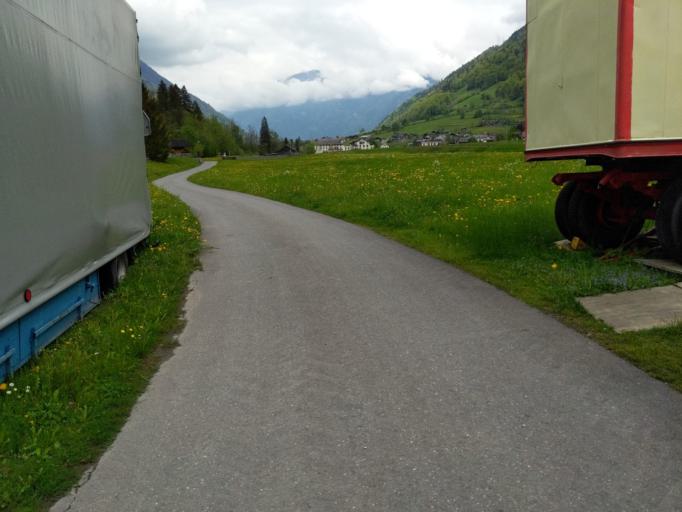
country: CH
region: Glarus
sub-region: Glarus
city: Luchsingen
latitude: 46.9463
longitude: 9.0232
